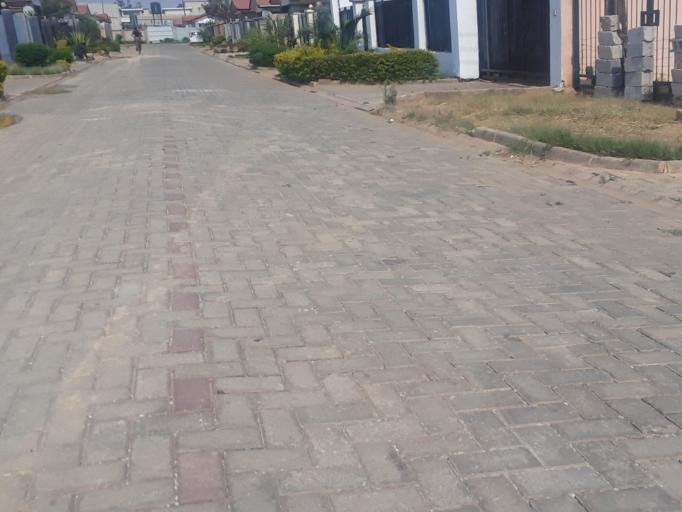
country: ZM
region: Lusaka
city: Lusaka
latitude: -15.3604
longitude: 28.2811
